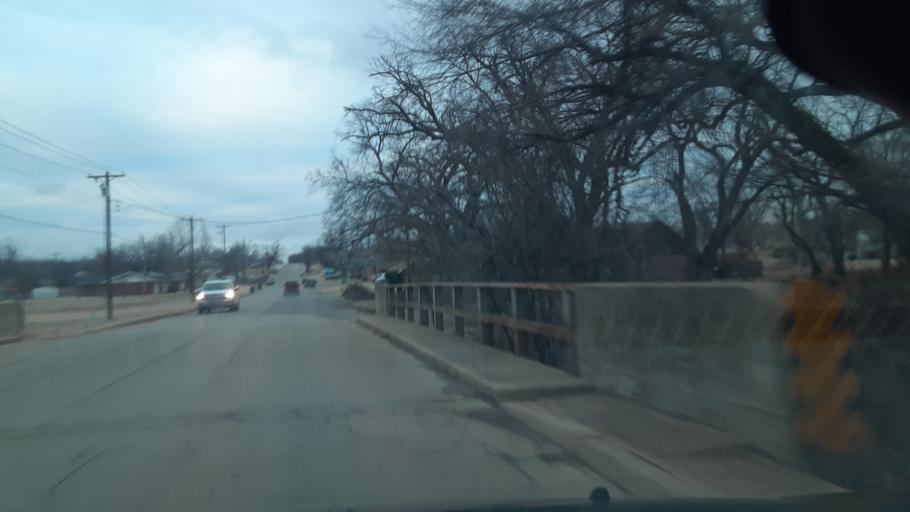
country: US
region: Oklahoma
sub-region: Logan County
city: Guthrie
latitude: 35.8871
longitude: -97.4163
